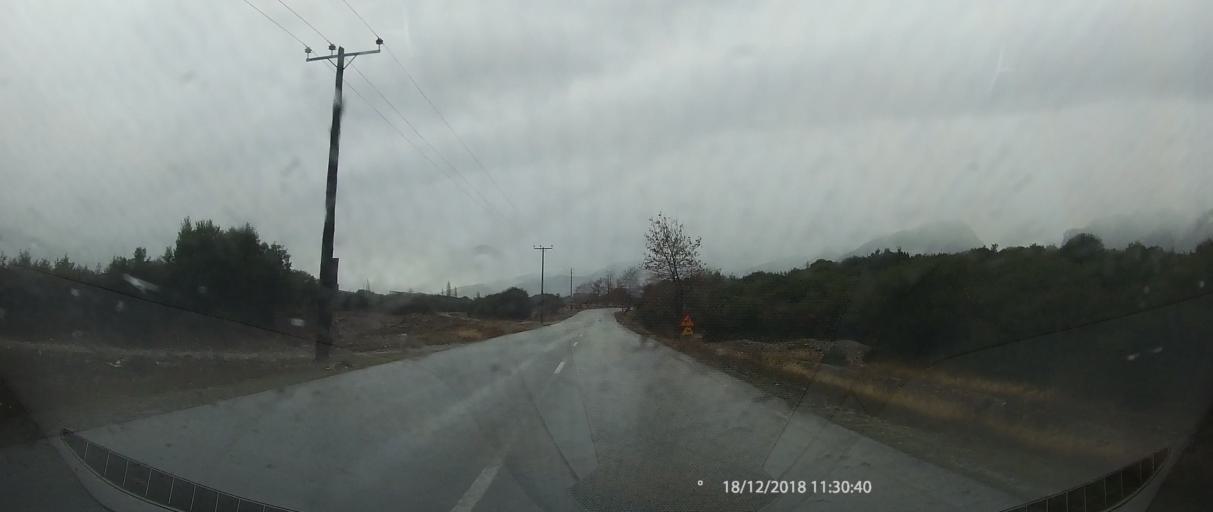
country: GR
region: Central Macedonia
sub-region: Nomos Pierias
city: Litochoro
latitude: 40.1200
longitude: 22.5194
